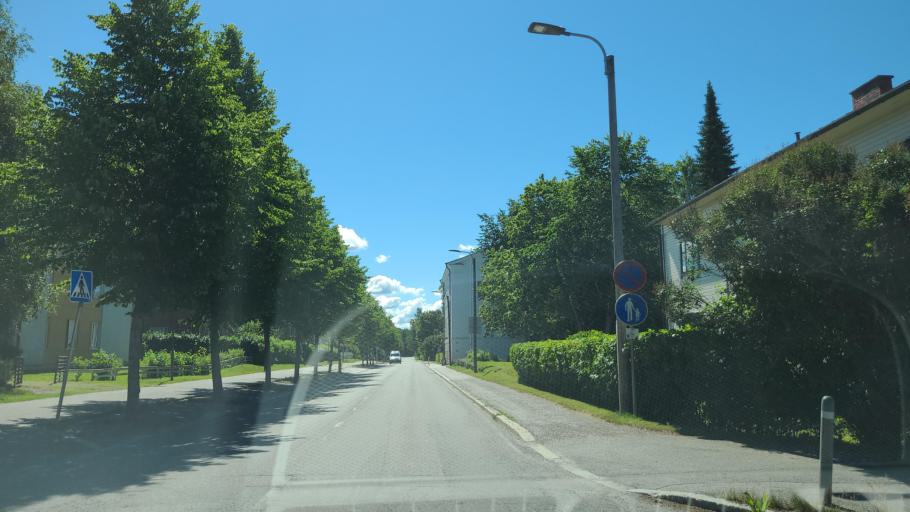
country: FI
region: Ostrobothnia
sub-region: Vaasa
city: Ristinummi
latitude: 63.0731
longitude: 21.7223
